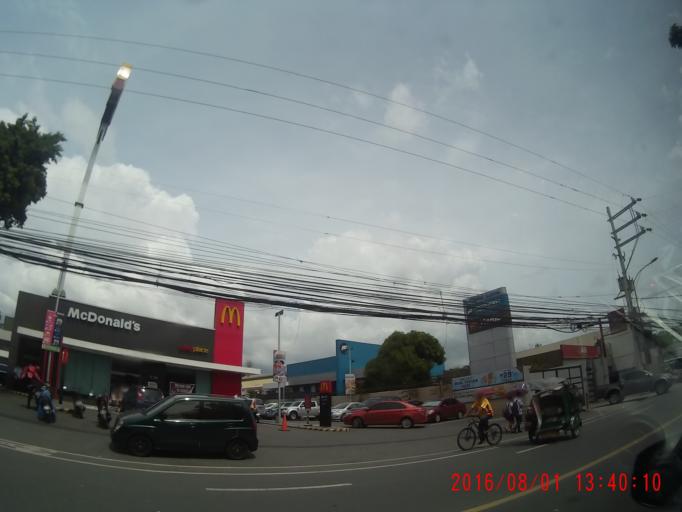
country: PH
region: Metro Manila
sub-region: Pasig
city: Pasig City
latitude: 14.5710
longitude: 121.0824
